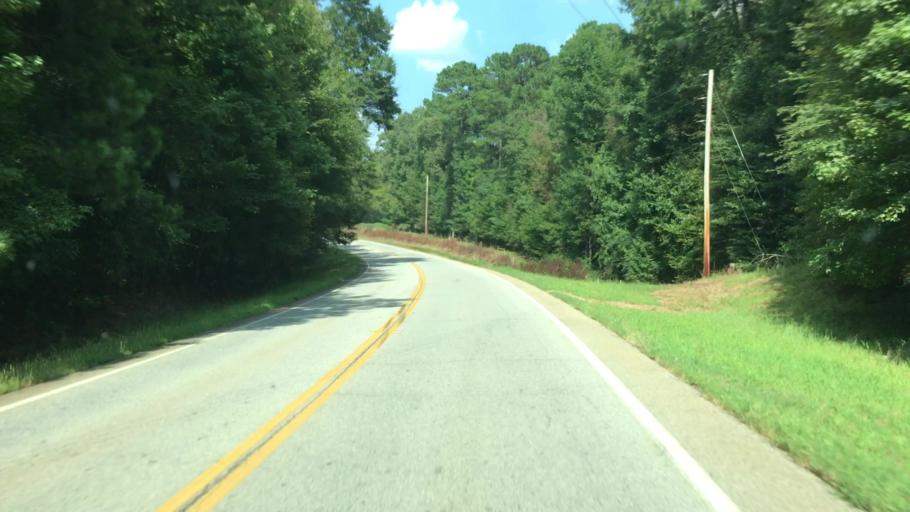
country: US
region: Georgia
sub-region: Butts County
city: Indian Springs
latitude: 33.1395
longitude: -83.8560
